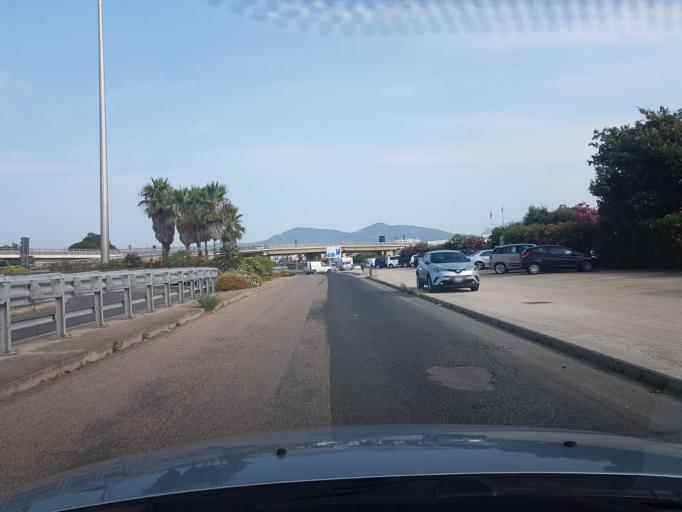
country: IT
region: Sardinia
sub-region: Provincia di Olbia-Tempio
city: Olbia
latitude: 40.9255
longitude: 9.5088
